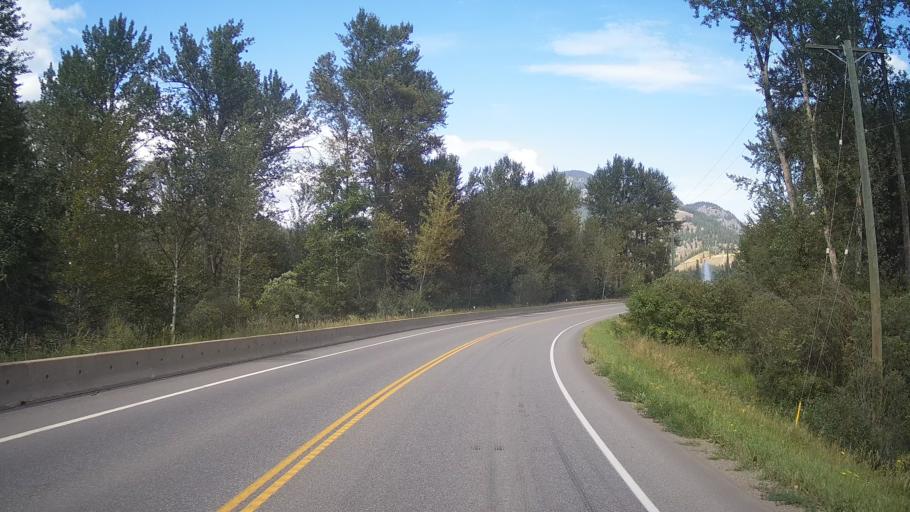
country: CA
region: British Columbia
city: Kamloops
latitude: 51.4144
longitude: -120.2133
